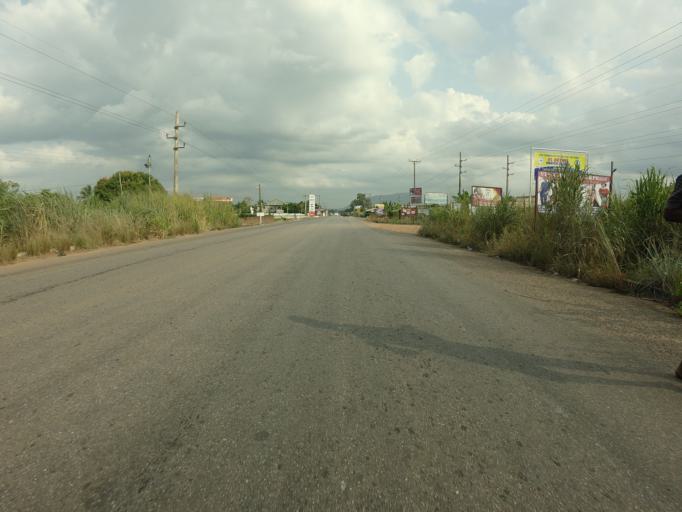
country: GH
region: Volta
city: Ho
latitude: 6.5851
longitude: 0.4800
